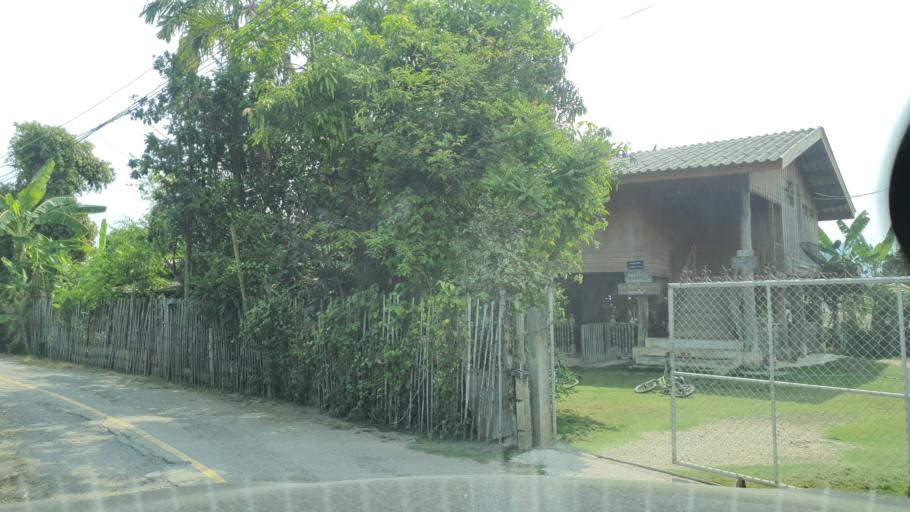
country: TH
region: Chiang Mai
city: Mae On
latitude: 18.7344
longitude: 99.2057
